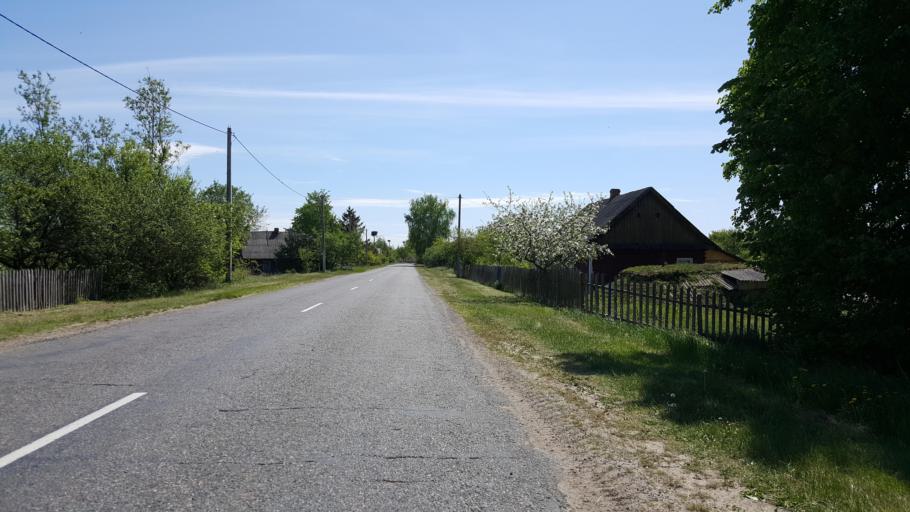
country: BY
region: Brest
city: Zhabinka
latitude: 52.3650
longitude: 24.1475
